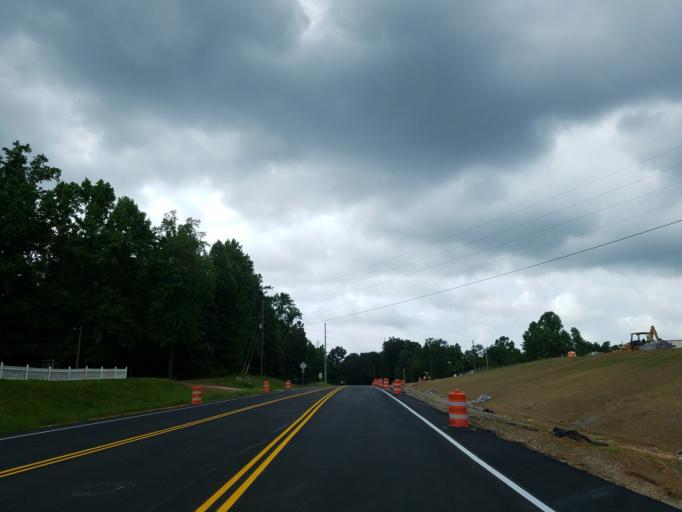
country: US
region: Georgia
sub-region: Dawson County
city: Dawsonville
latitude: 34.4289
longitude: -84.1602
